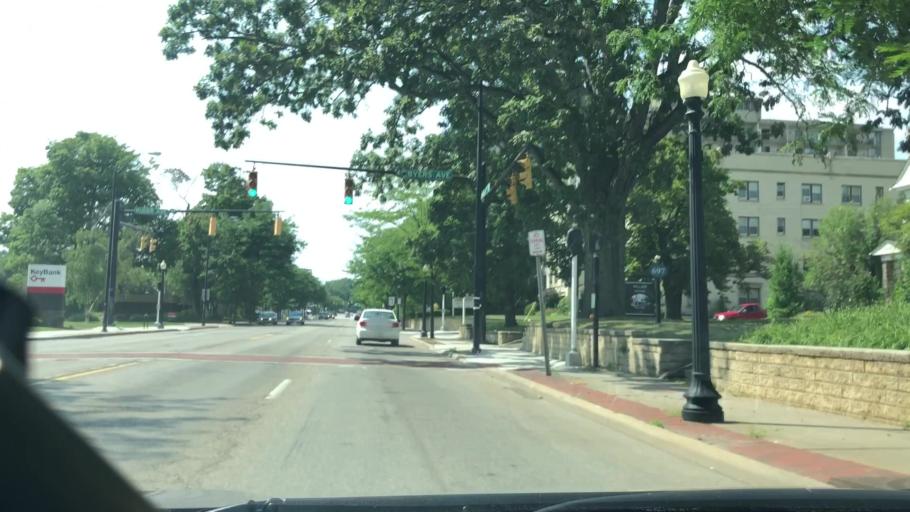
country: US
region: Ohio
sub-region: Summit County
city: Akron
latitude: 41.0949
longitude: -81.5396
